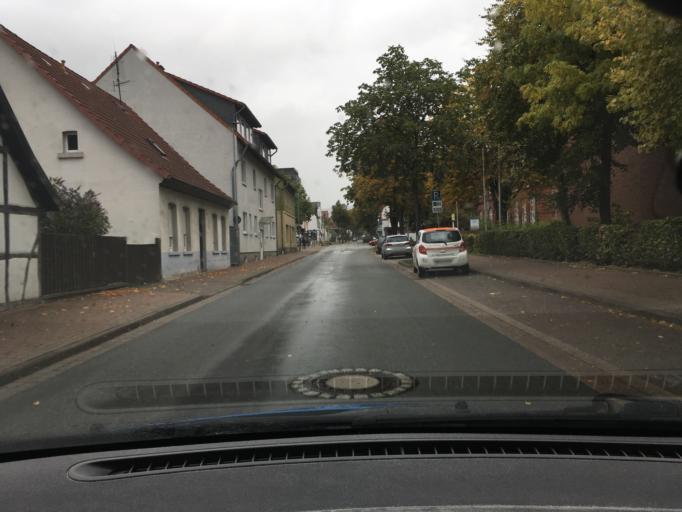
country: DE
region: Lower Saxony
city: Springe
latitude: 52.2088
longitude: 9.5587
